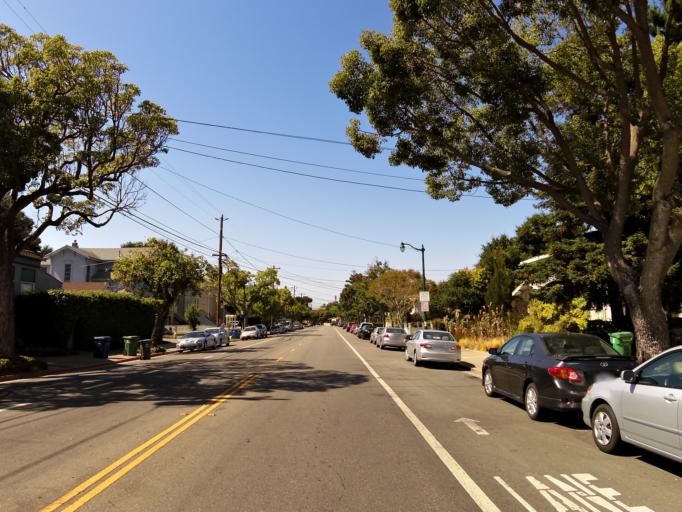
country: US
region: California
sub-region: Alameda County
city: Alameda
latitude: 37.7716
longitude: -122.2563
